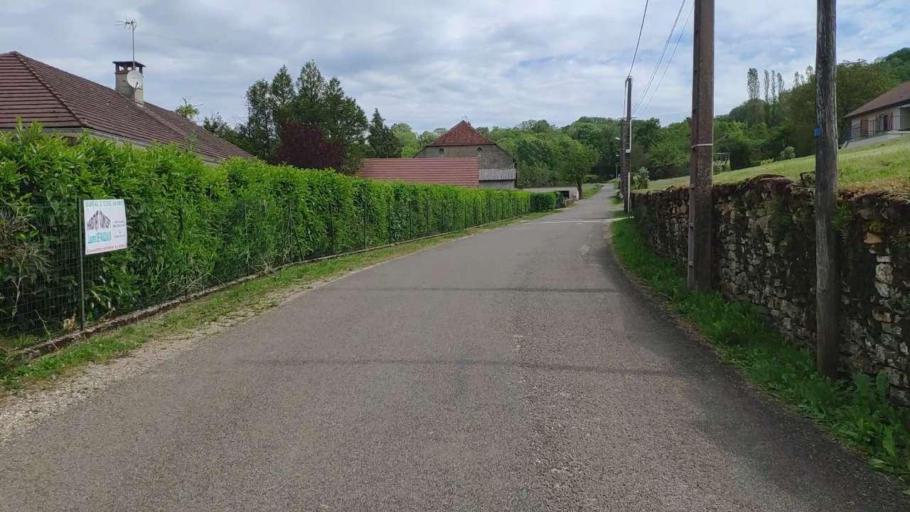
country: FR
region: Franche-Comte
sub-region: Departement du Jura
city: Poligny
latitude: 46.7703
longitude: 5.6235
